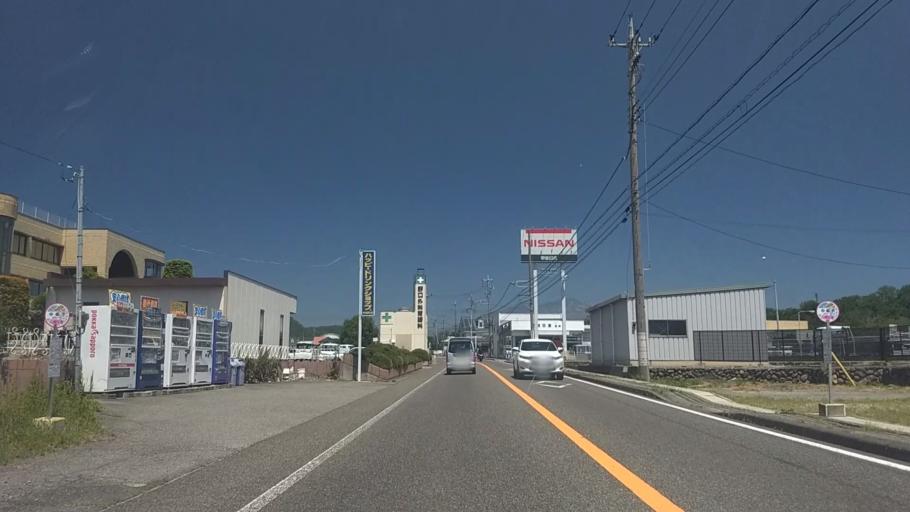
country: JP
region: Yamanashi
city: Nirasaki
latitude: 35.7441
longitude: 138.4413
